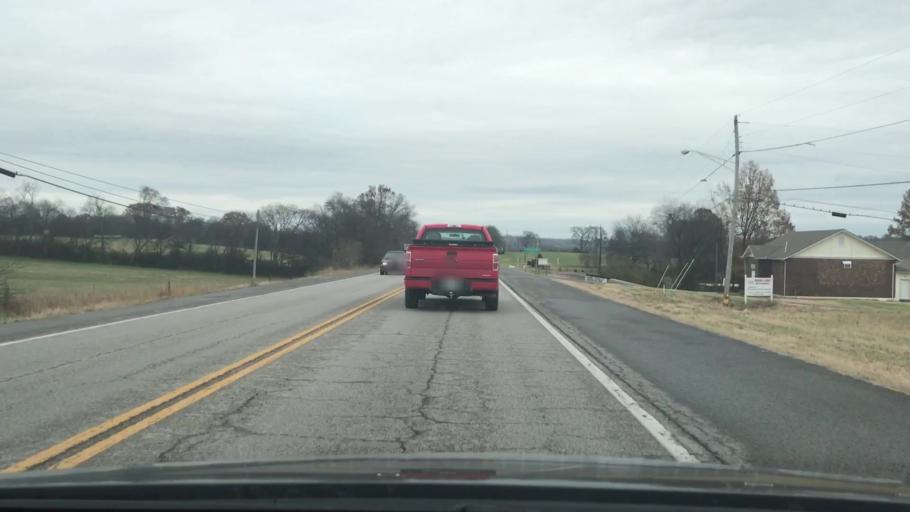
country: US
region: Tennessee
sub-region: Sumner County
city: Gallatin
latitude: 36.3971
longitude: -86.3270
